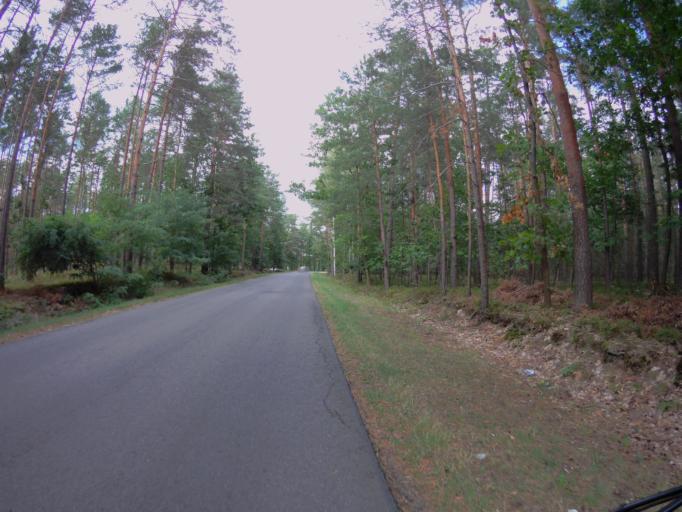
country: PL
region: Subcarpathian Voivodeship
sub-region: Powiat lezajski
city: Brzoza Krolewska
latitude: 50.2473
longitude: 22.3650
